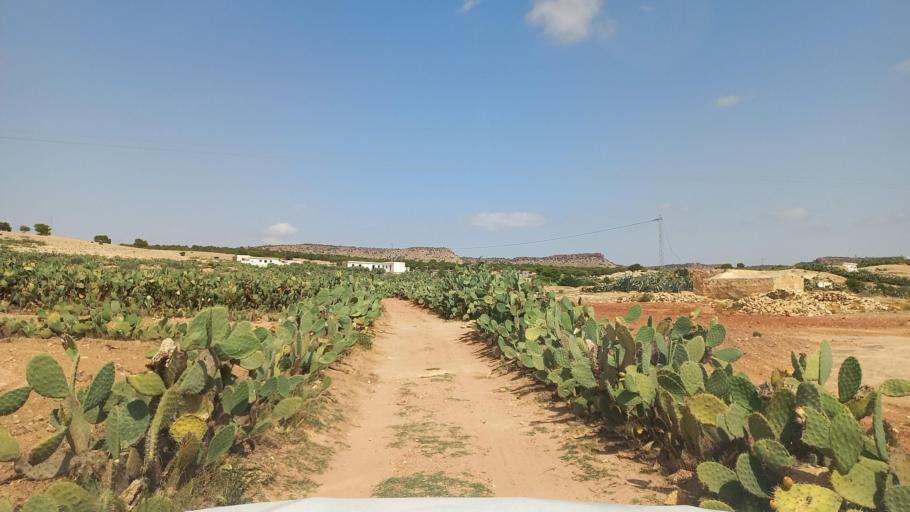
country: TN
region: Al Qasrayn
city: Sbiba
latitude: 35.4008
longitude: 8.9697
